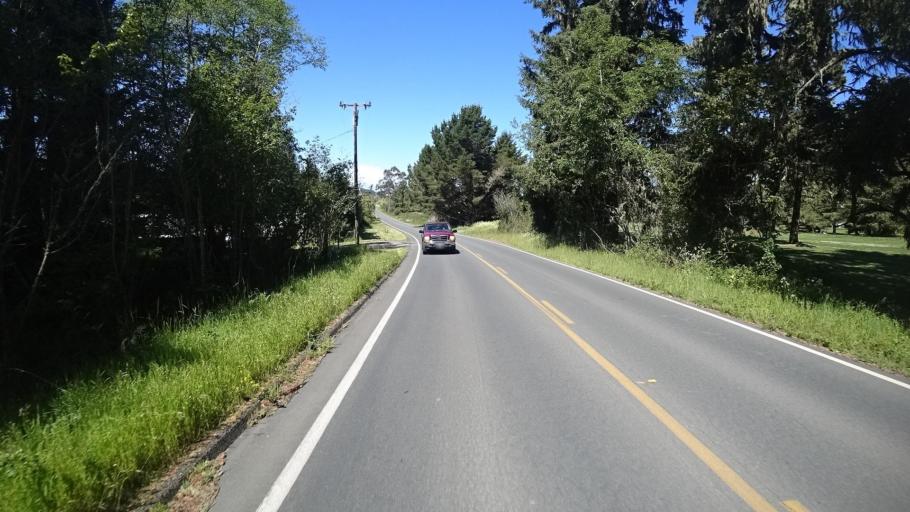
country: US
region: California
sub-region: Humboldt County
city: McKinleyville
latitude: 40.9569
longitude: -124.0903
